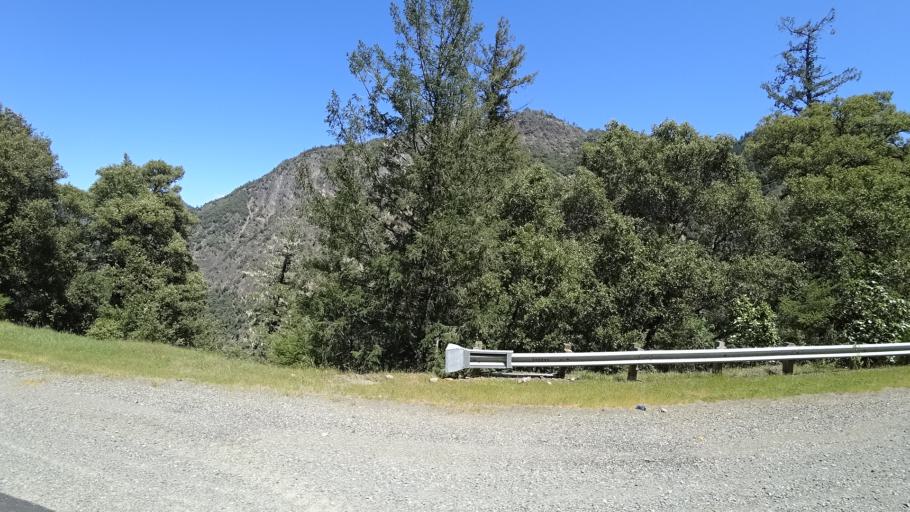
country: US
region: California
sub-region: Humboldt County
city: Willow Creek
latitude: 40.8176
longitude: -123.4790
